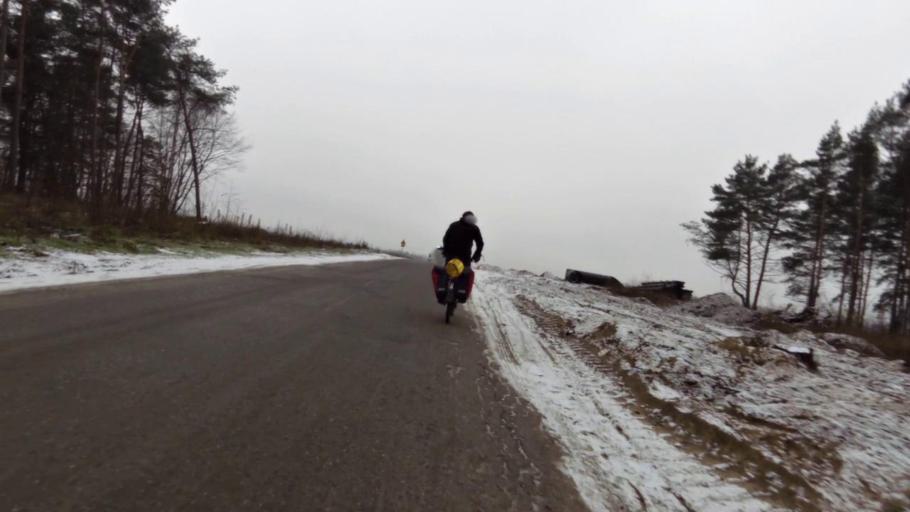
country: PL
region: West Pomeranian Voivodeship
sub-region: Powiat walecki
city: Walcz
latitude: 53.2965
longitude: 16.4771
